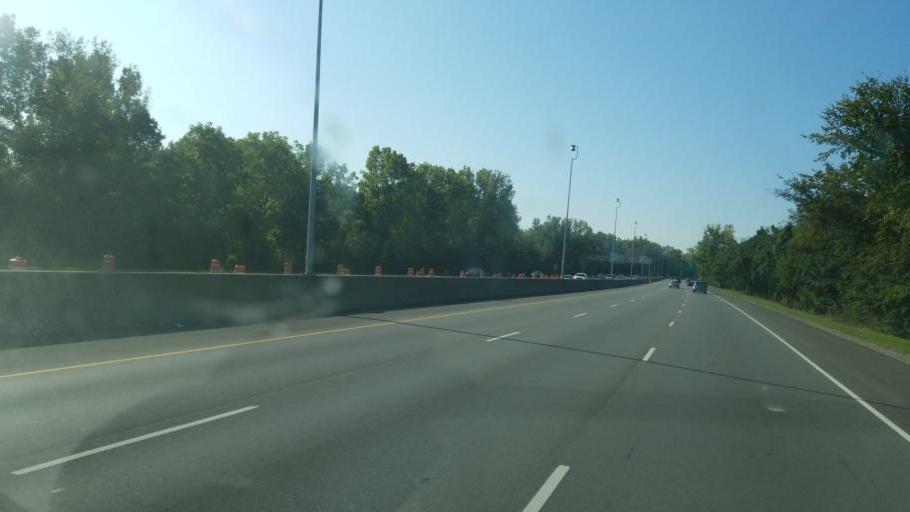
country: US
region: Ohio
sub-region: Franklin County
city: Worthington
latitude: 40.1003
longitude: -83.0368
